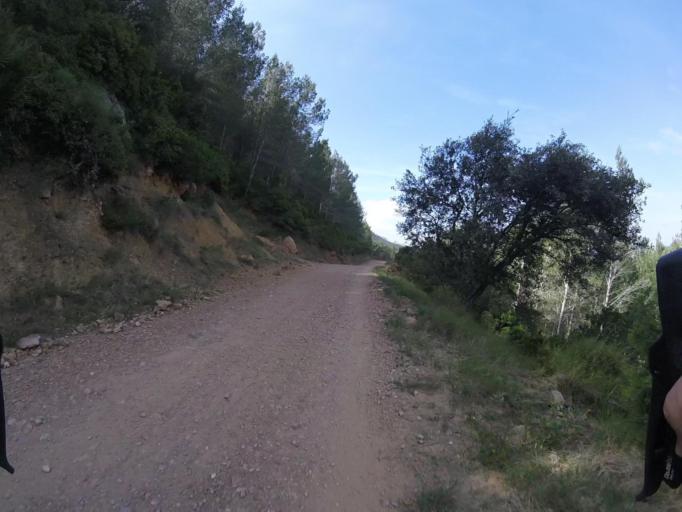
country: ES
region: Valencia
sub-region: Provincia de Castello
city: Benicassim
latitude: 40.0990
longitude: 0.0416
